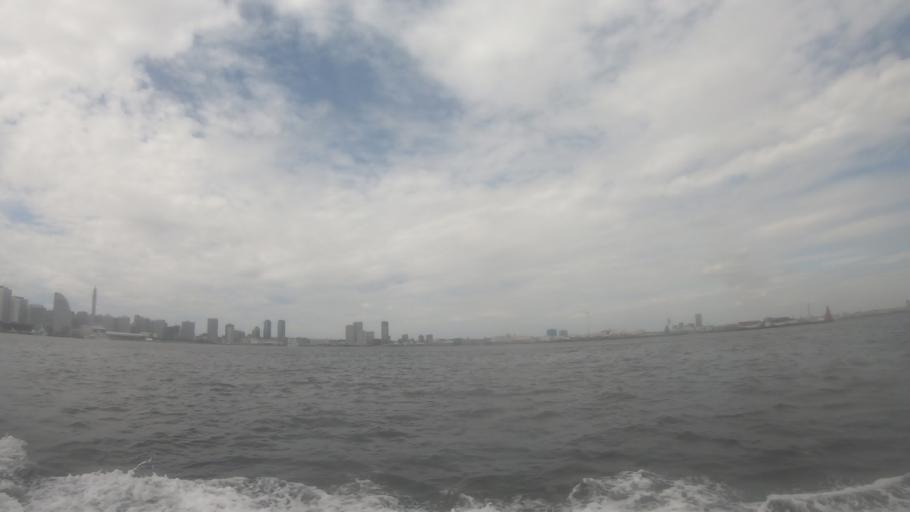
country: JP
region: Kanagawa
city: Yokohama
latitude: 35.4558
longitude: 139.6575
